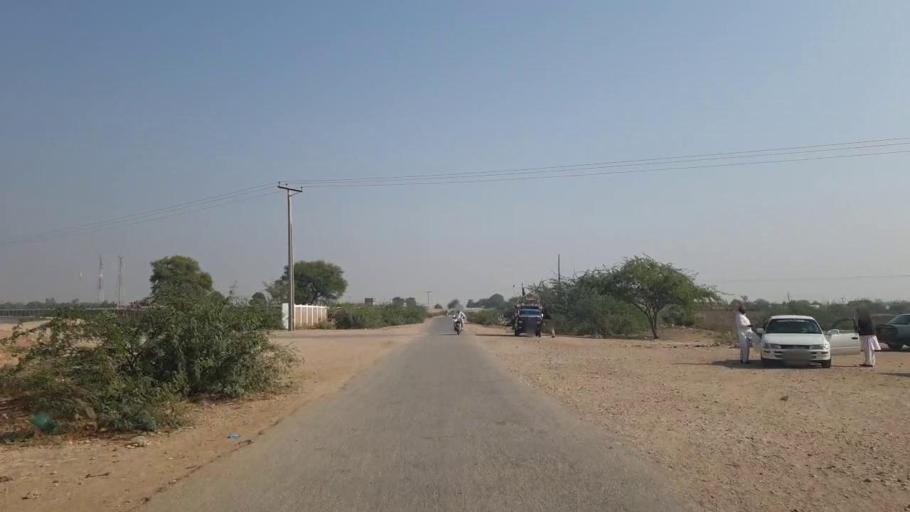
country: PK
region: Sindh
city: Jamshoro
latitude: 25.5312
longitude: 68.3207
